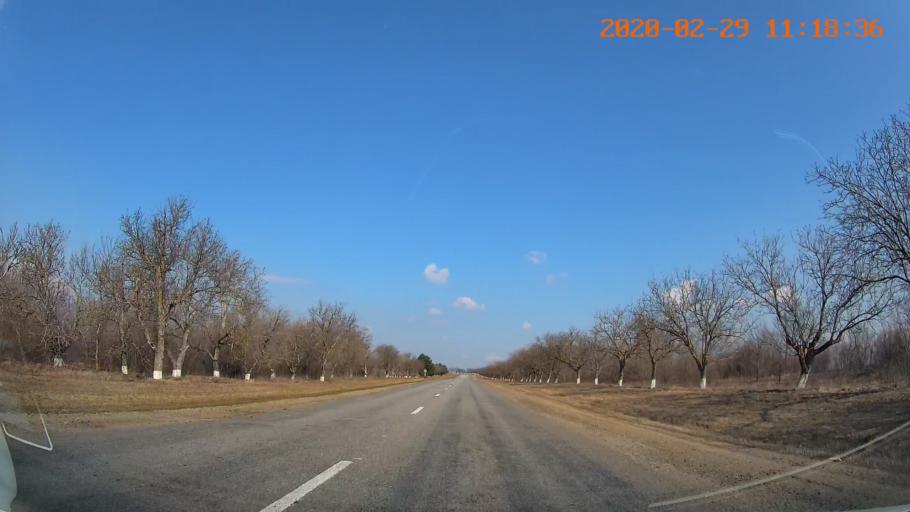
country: MD
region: Telenesti
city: Cocieri
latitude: 47.3372
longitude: 29.1742
